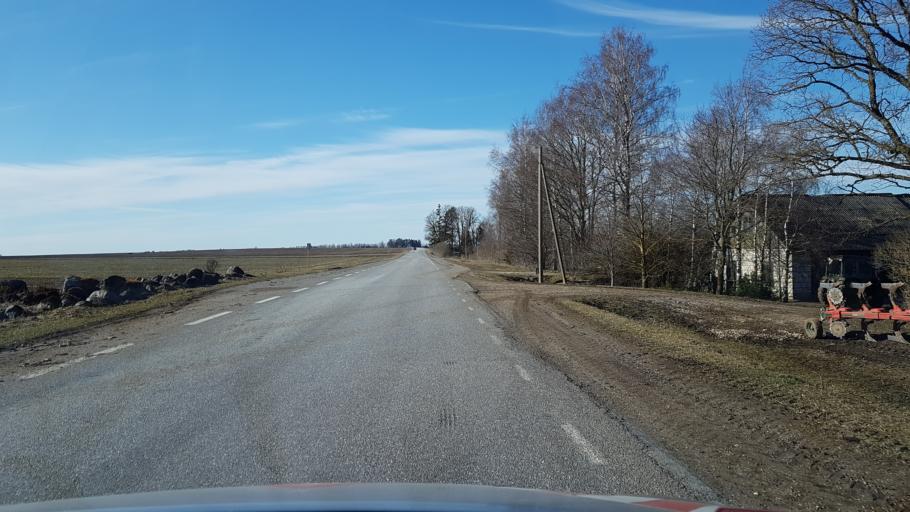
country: EE
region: Laeaene-Virumaa
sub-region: Kadrina vald
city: Kadrina
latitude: 59.3236
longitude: 26.1425
